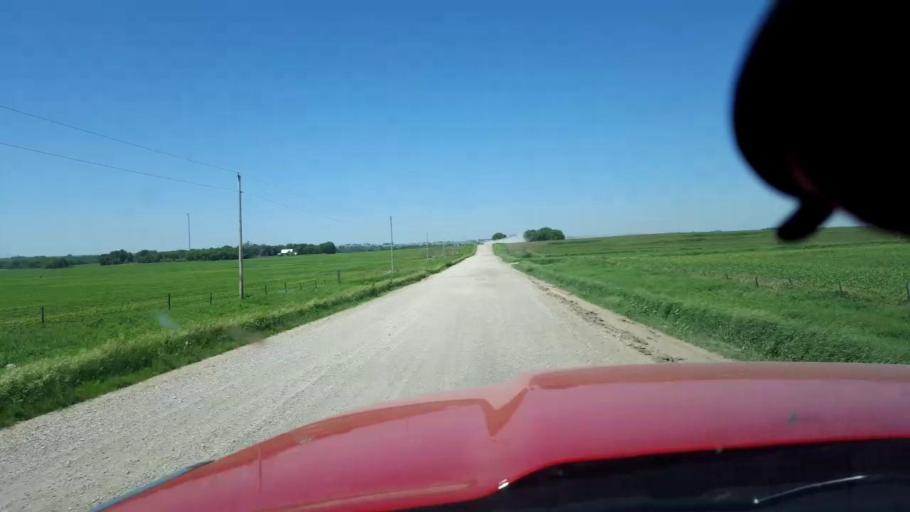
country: US
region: Iowa
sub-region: Chickasaw County
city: New Hampton
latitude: 43.2135
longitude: -92.2459
